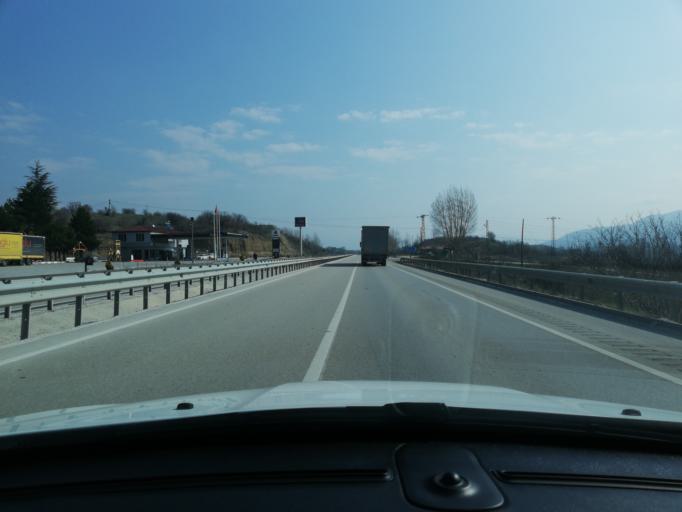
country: TR
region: Cankiri
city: Beloren
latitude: 40.8690
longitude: 33.4909
